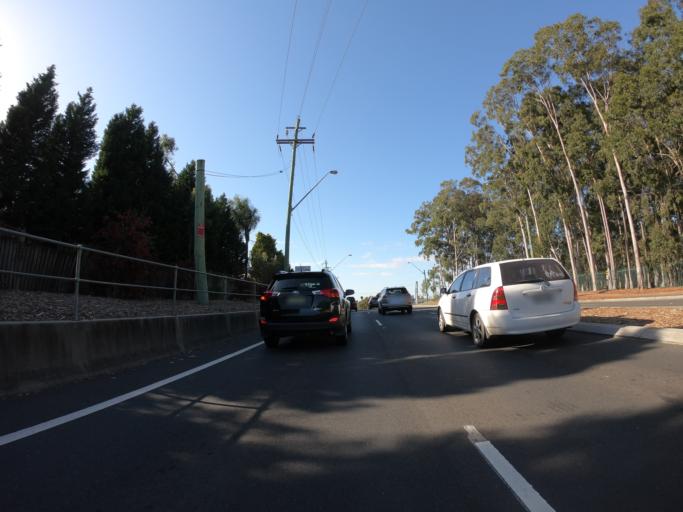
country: AU
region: New South Wales
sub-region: The Hills Shire
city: Castle Hill
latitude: -33.7239
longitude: 150.9765
